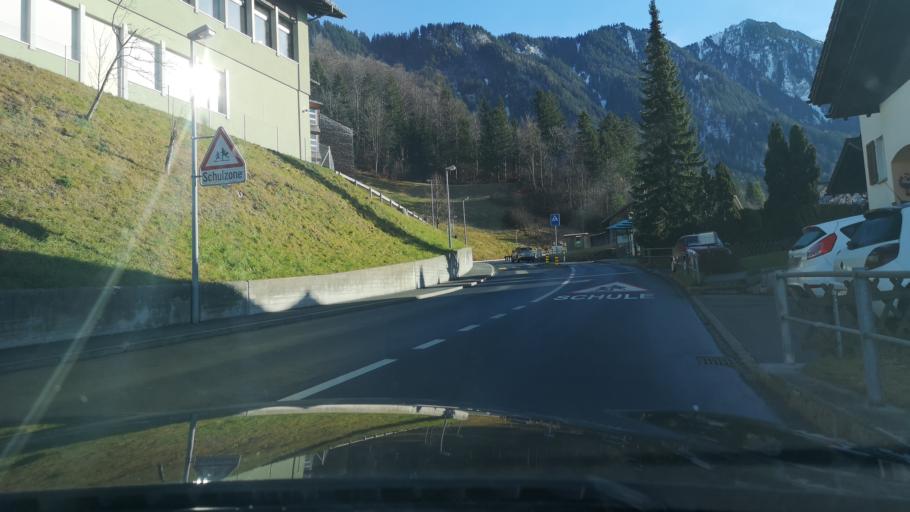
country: LI
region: Triesenberg
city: Triesenberg
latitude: 47.1172
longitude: 9.5462
